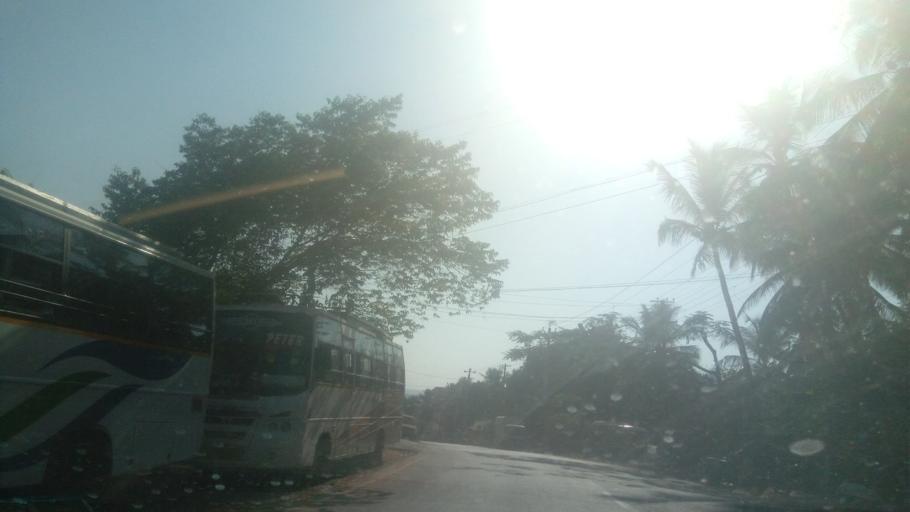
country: IN
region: Goa
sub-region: North Goa
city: Jua
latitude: 15.5176
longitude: 73.9622
